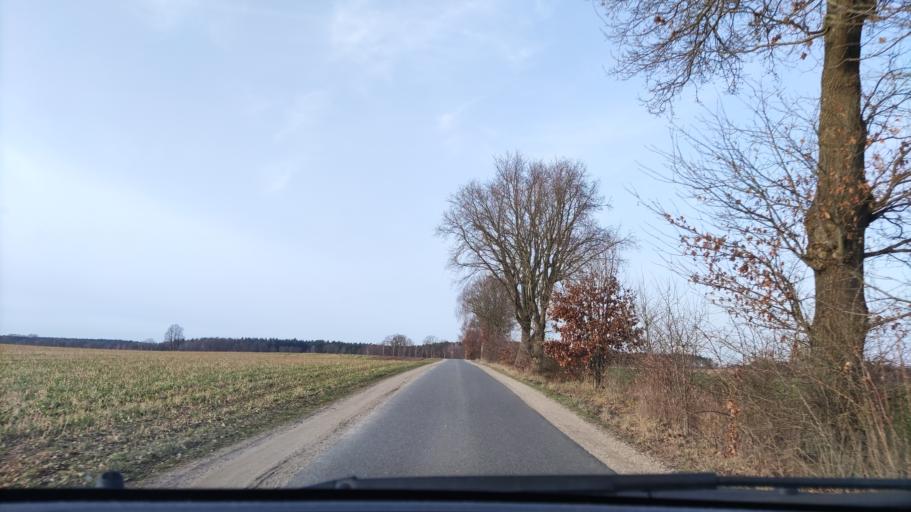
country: DE
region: Lower Saxony
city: Dahlenburg
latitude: 53.1901
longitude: 10.6977
